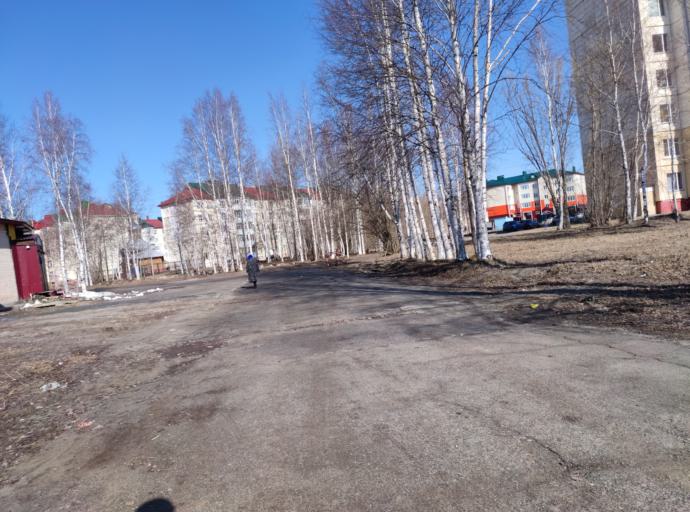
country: RU
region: Khanty-Mansiyskiy Avtonomnyy Okrug
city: Langepas
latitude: 61.2512
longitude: 75.1722
